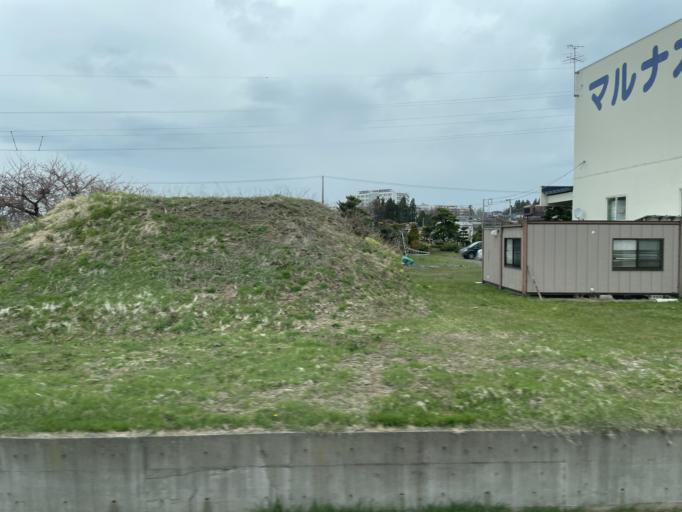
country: JP
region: Aomori
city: Namioka
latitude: 40.7064
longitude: 140.5770
